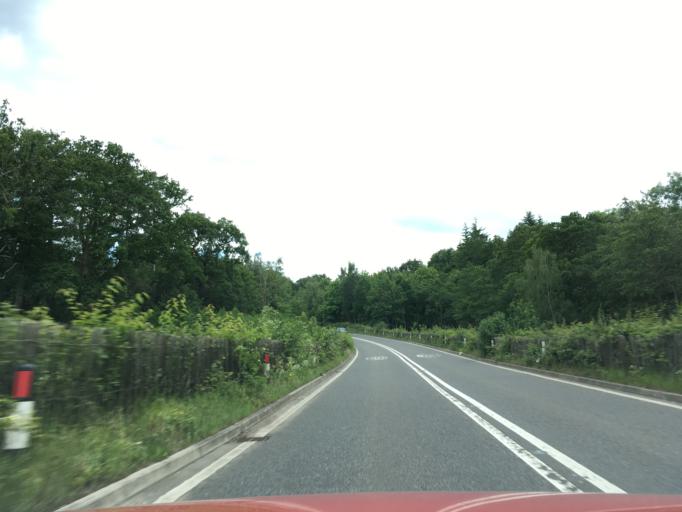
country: GB
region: England
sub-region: Oxfordshire
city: Boars Hill
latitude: 51.7168
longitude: -1.2668
